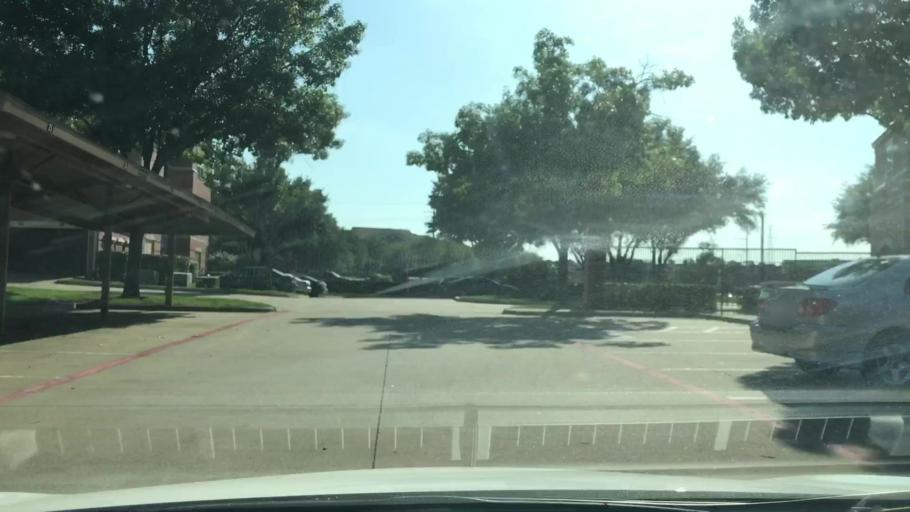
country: US
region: Texas
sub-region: Dallas County
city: Farmers Branch
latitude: 32.9258
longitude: -96.9570
